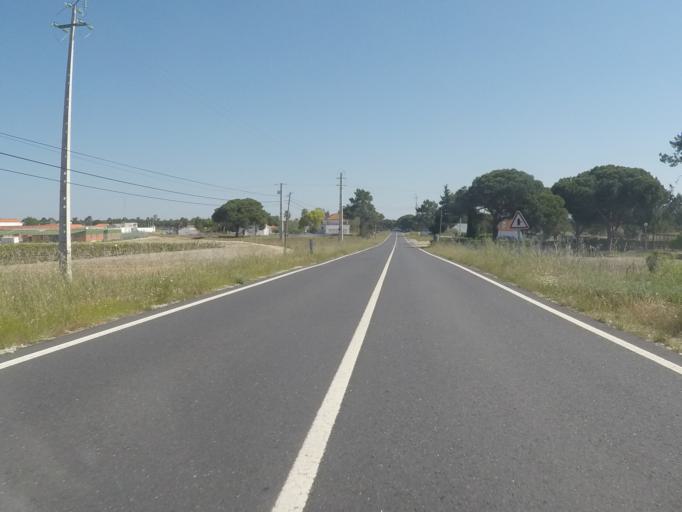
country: PT
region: Setubal
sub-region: Grandola
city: Grandola
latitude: 38.2646
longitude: -8.7295
